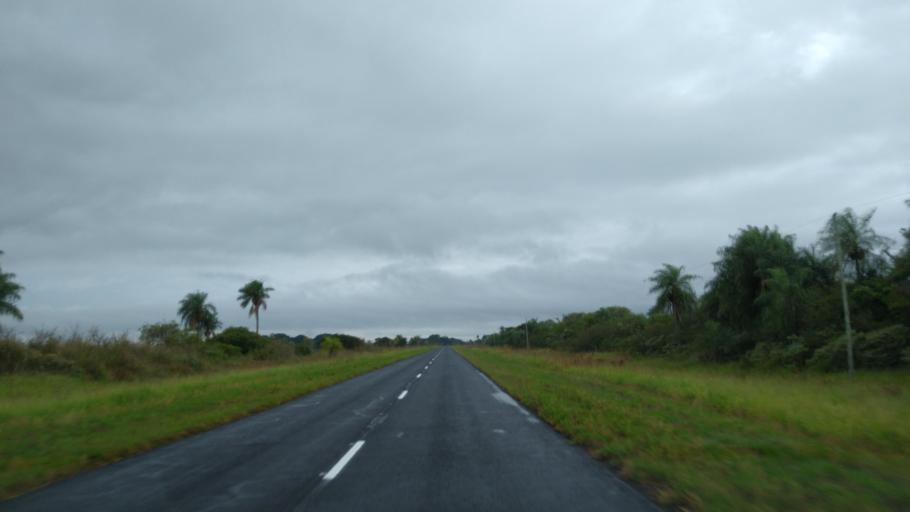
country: AR
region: Corrientes
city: Loreto
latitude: -27.6997
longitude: -57.2232
